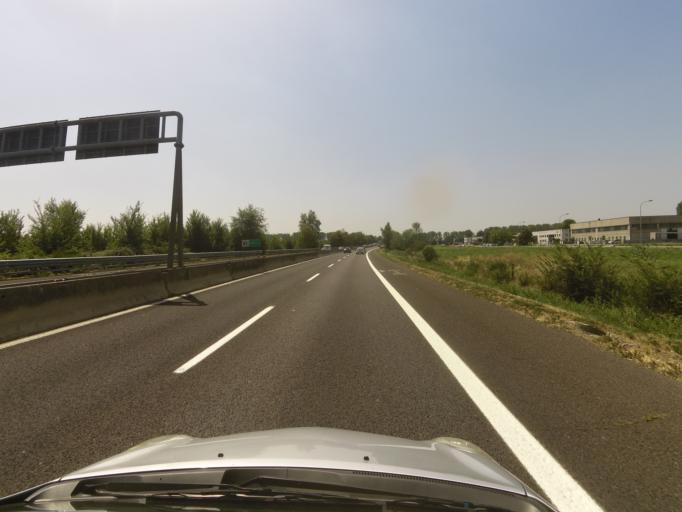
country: IT
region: Emilia-Romagna
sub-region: Provincia di Ferrara
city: Porotto-Cassama
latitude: 44.8589
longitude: 11.5698
